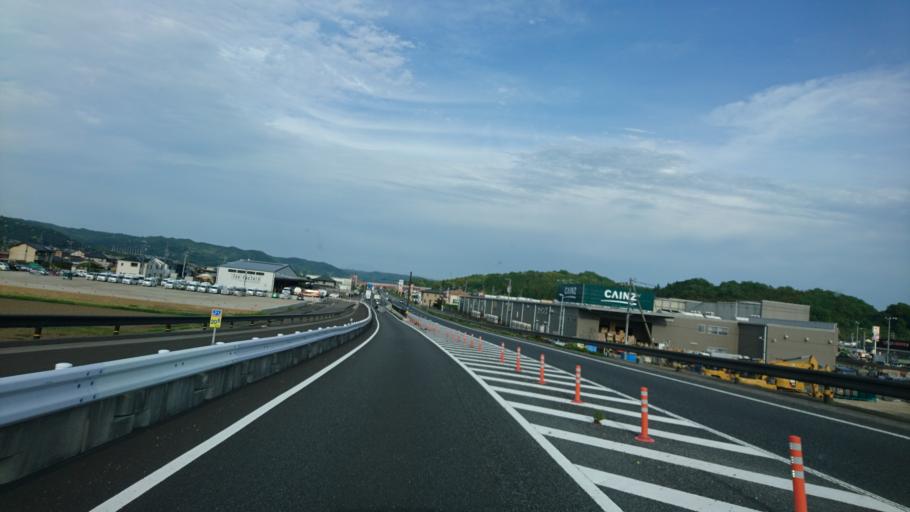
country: JP
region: Gifu
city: Mitake
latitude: 35.4304
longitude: 137.0839
